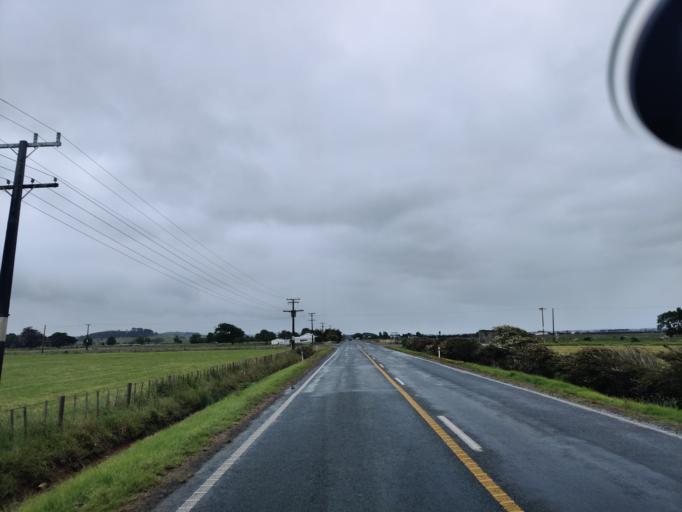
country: NZ
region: Northland
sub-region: Kaipara District
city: Dargaville
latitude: -35.9509
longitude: 173.8919
